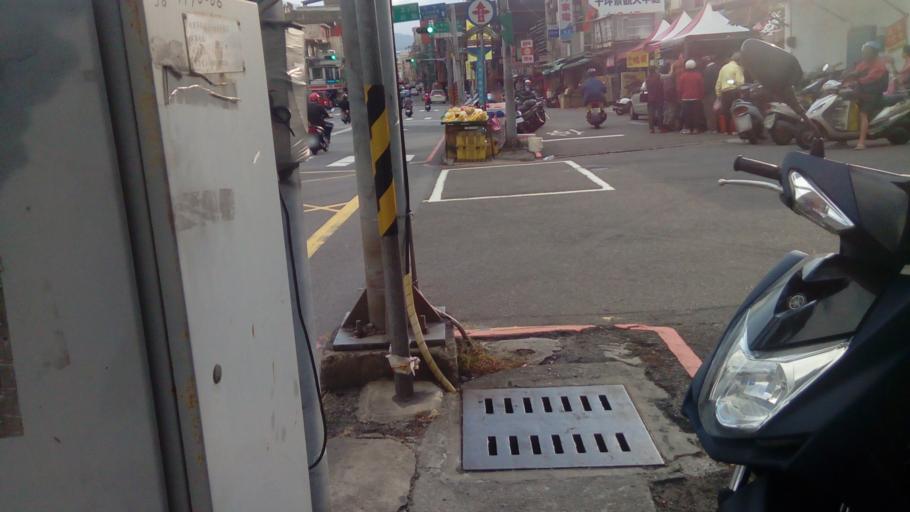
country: TW
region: Taipei
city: Taipei
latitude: 25.1775
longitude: 121.4432
